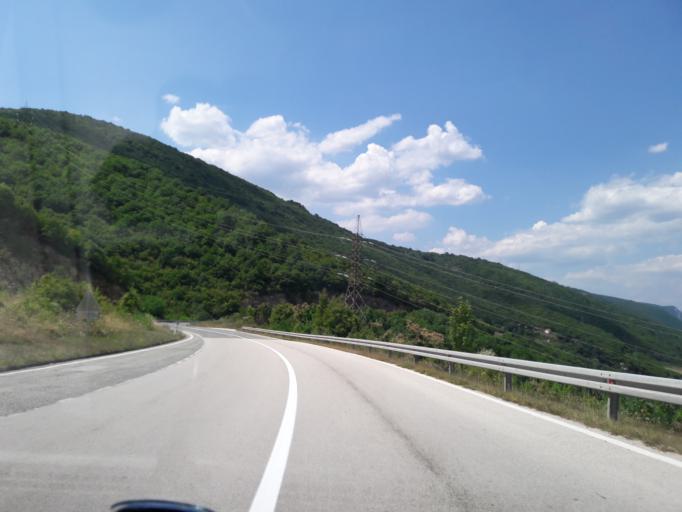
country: BA
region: Republika Srpska
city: Mrkonjic Grad
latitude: 44.5098
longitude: 17.1558
